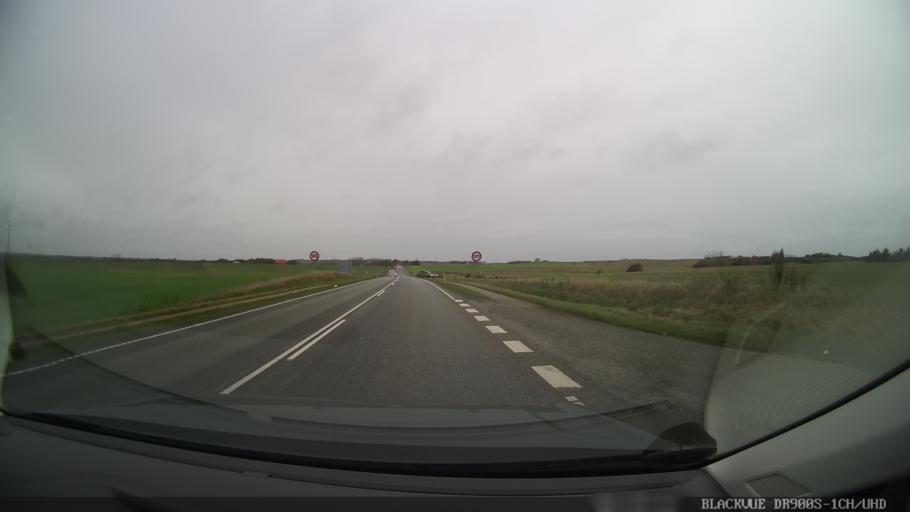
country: DK
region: North Denmark
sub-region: Thisted Kommune
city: Thisted
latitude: 56.8568
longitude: 8.6953
